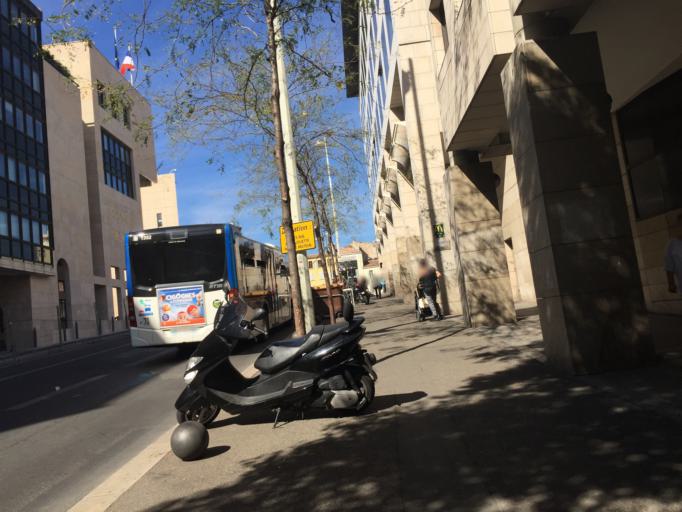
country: FR
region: Provence-Alpes-Cote d'Azur
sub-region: Departement des Bouches-du-Rhone
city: Marseille 03
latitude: 43.3009
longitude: 5.3742
